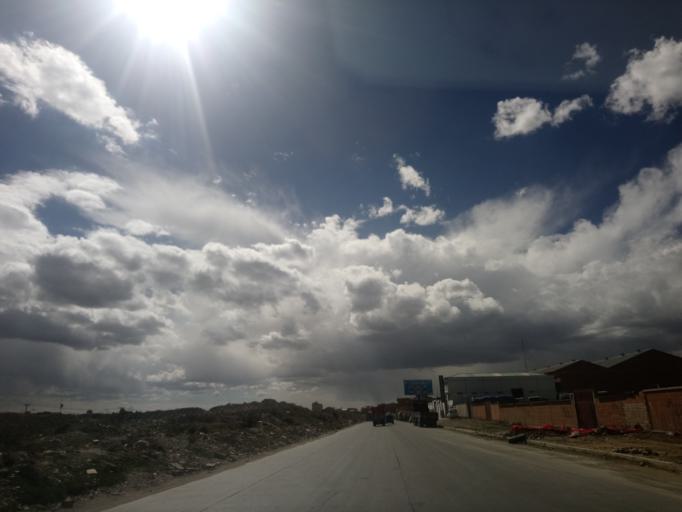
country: BO
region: La Paz
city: La Paz
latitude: -16.5532
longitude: -68.1821
